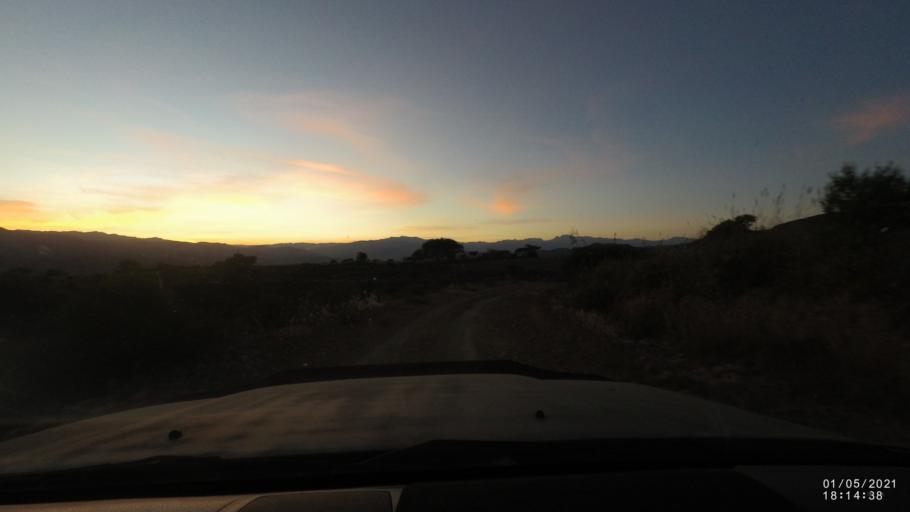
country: BO
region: Cochabamba
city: Capinota
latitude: -17.6739
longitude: -66.2130
